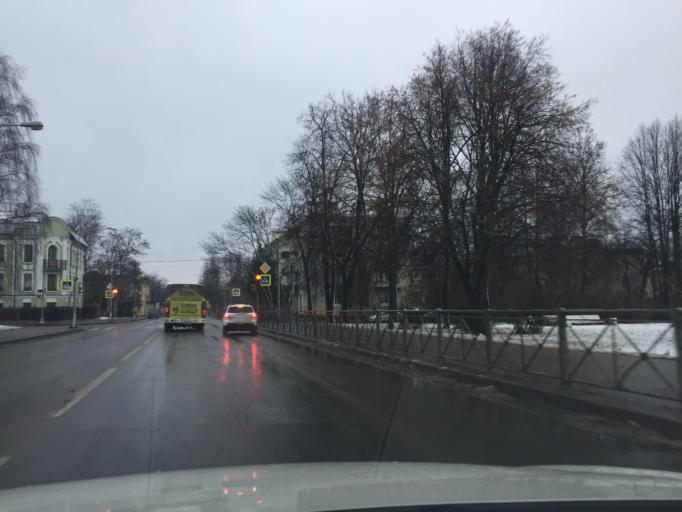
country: RU
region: St.-Petersburg
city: Pushkin
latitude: 59.7151
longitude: 30.4075
